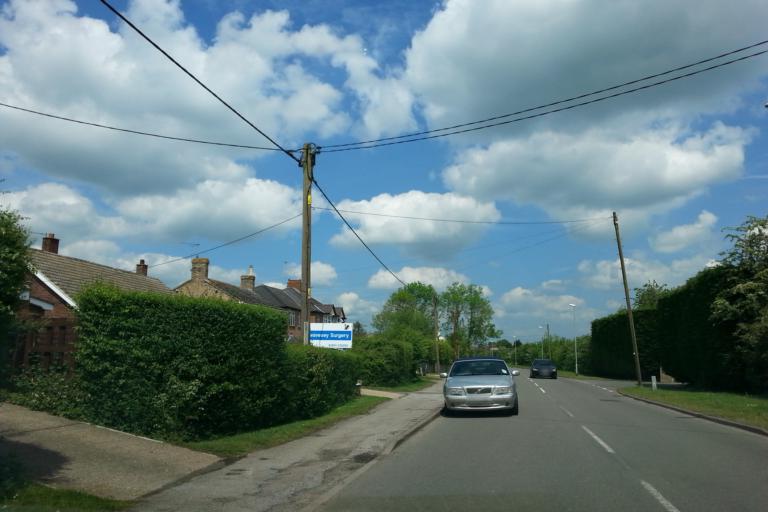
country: GB
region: England
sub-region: Cambridgeshire
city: Swavesey
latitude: 52.2887
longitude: -0.0032
